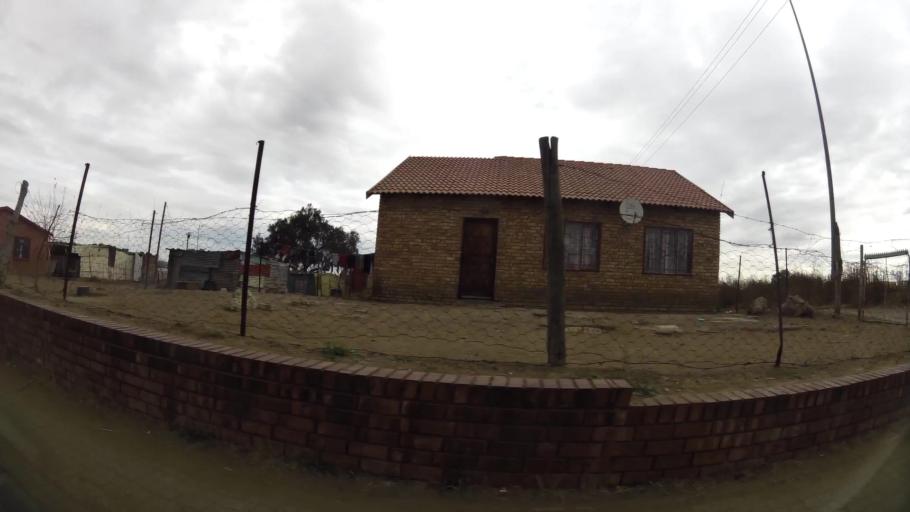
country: ZA
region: Orange Free State
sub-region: Fezile Dabi District Municipality
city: Kroonstad
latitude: -27.6517
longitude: 27.2221
